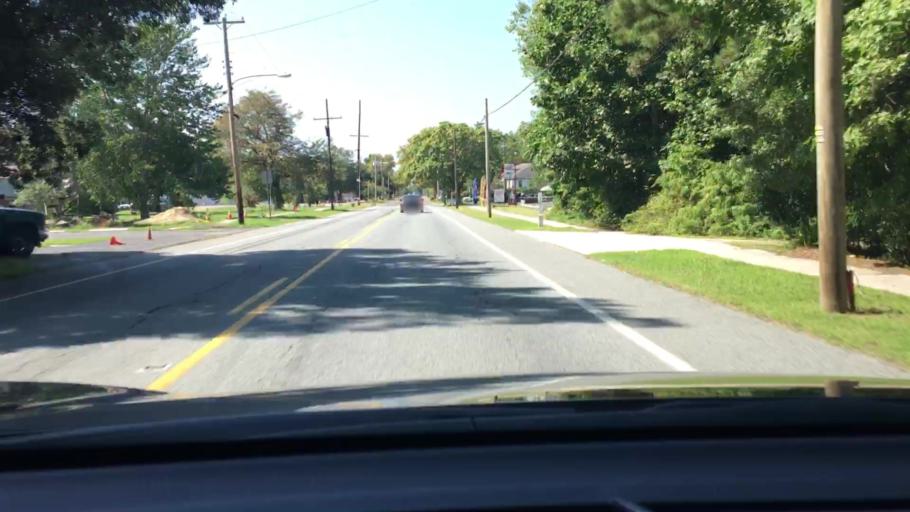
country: US
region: New Jersey
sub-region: Cape May County
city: Woodbine
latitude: 39.2460
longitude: -74.8116
